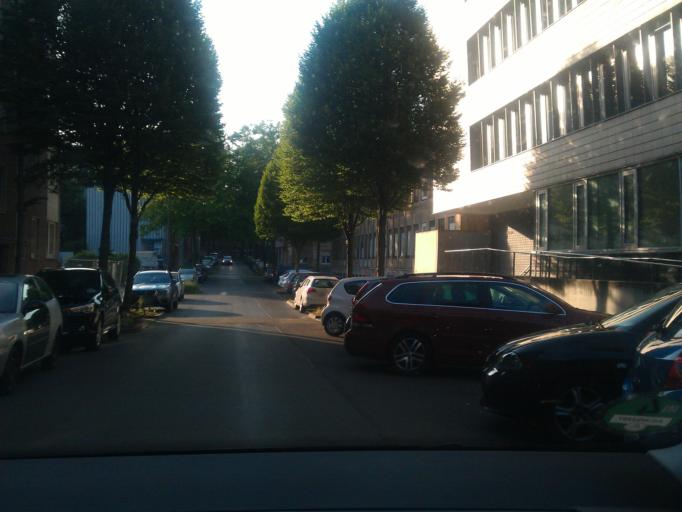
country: DE
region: North Rhine-Westphalia
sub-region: Regierungsbezirk Koln
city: Aachen
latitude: 50.7693
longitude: 6.0833
